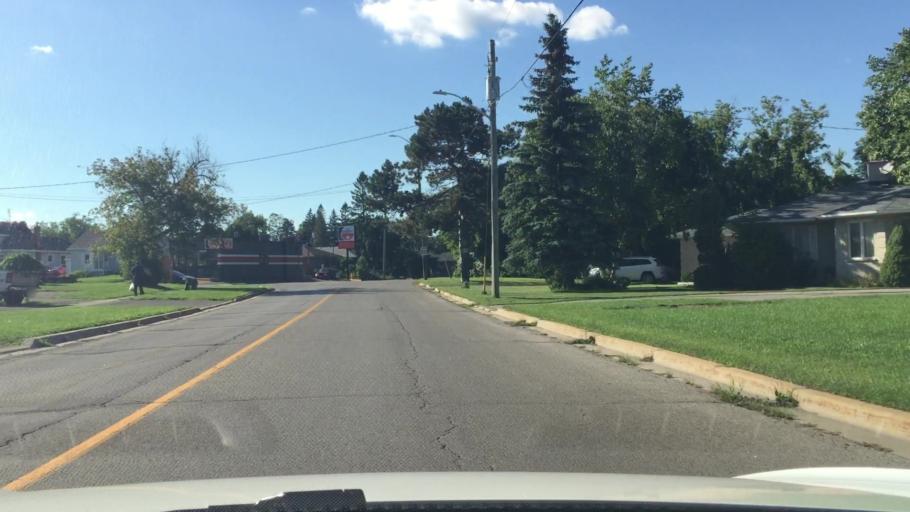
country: CA
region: Ontario
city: Oshawa
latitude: 43.9053
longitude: -78.8782
